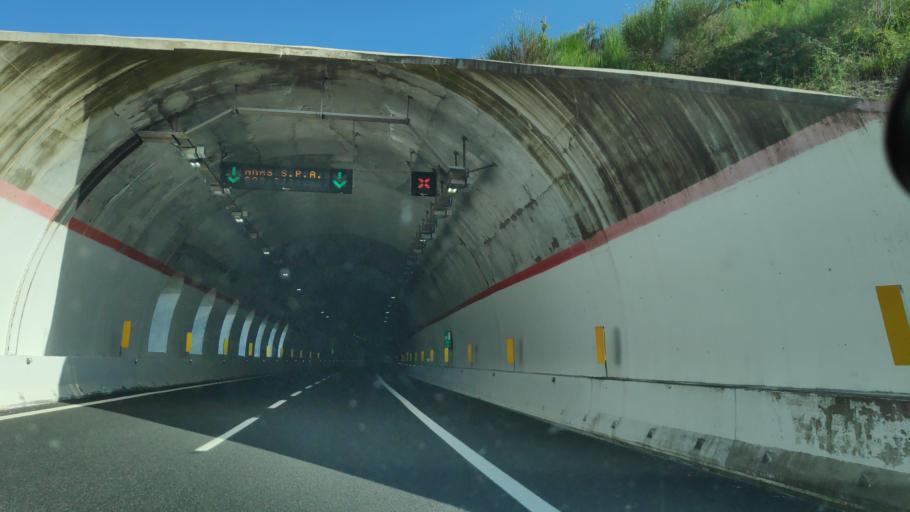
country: IT
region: Campania
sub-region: Provincia di Salerno
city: Casalbuono
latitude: 40.2281
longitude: 15.6696
